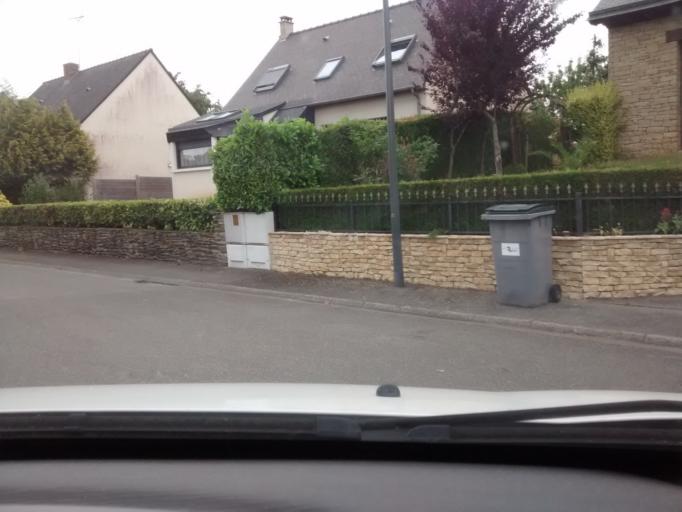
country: FR
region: Brittany
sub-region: Departement d'Ille-et-Vilaine
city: Cesson-Sevigne
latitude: 48.1272
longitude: -1.5990
